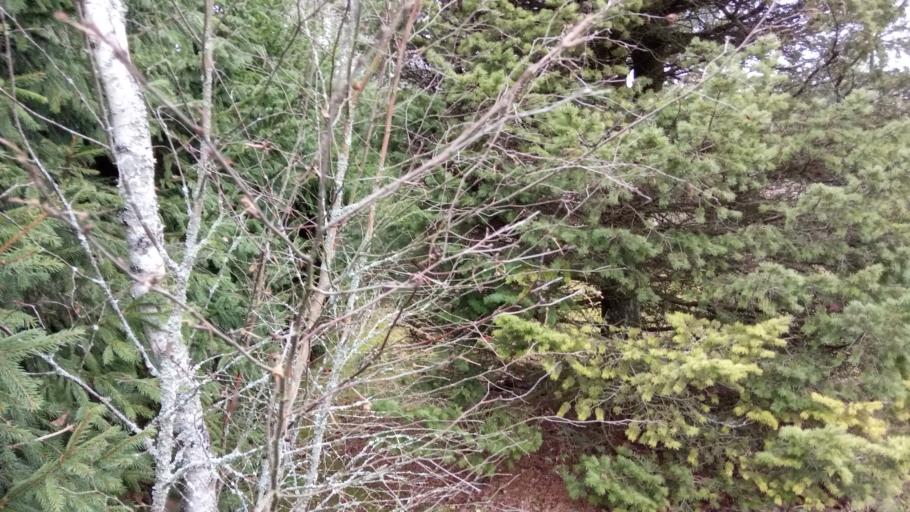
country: EE
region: Harju
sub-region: Kuusalu vald
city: Kuusalu
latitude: 59.4515
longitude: 25.4219
